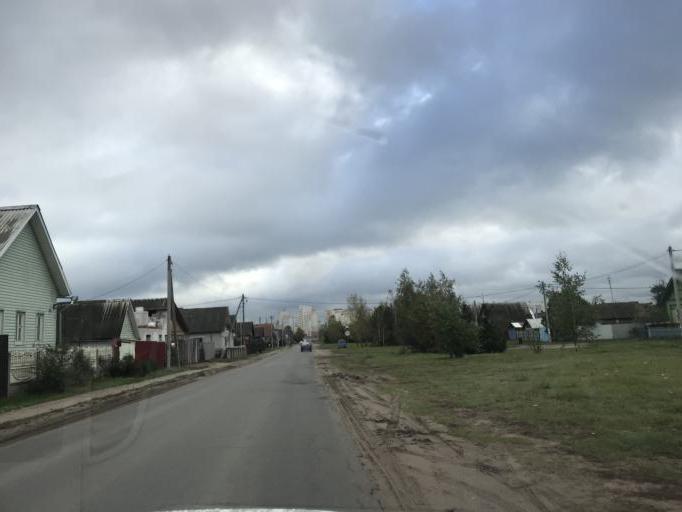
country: BY
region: Mogilev
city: Mahilyow
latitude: 53.8841
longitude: 30.3473
